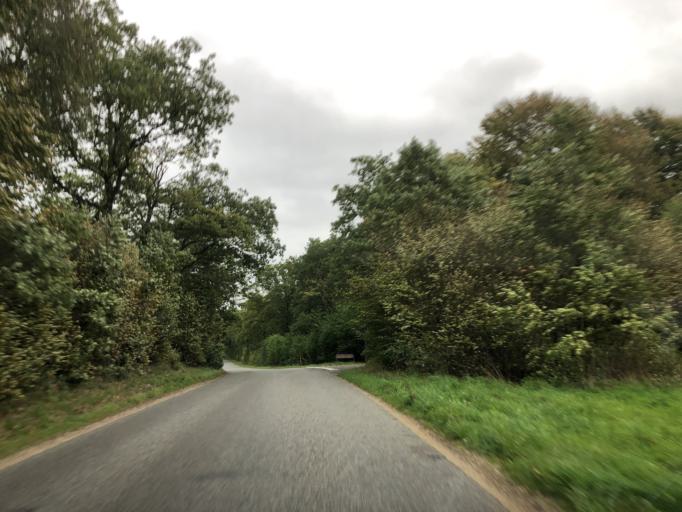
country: DK
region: Central Jutland
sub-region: Viborg Kommune
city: Viborg
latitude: 56.4229
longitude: 9.3363
